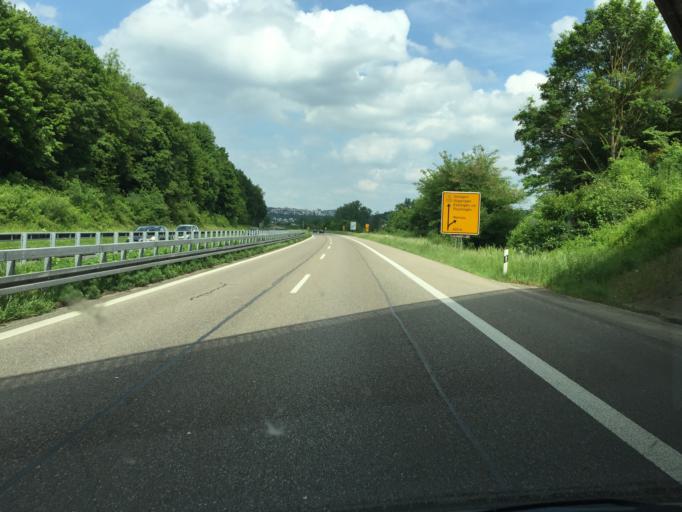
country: DE
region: Baden-Wuerttemberg
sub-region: Regierungsbezirk Stuttgart
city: Wernau
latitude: 48.6930
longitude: 9.3984
